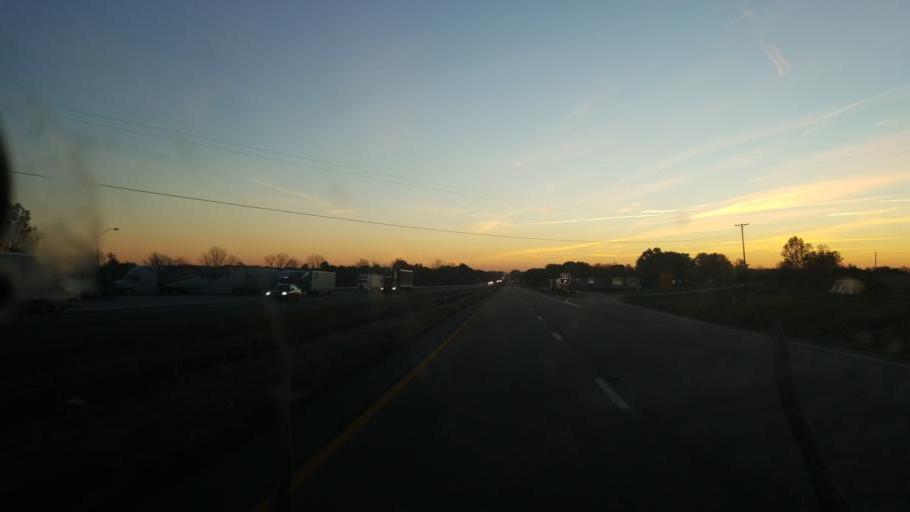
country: US
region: Missouri
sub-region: Cooper County
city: Boonville
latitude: 38.9367
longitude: -92.7303
